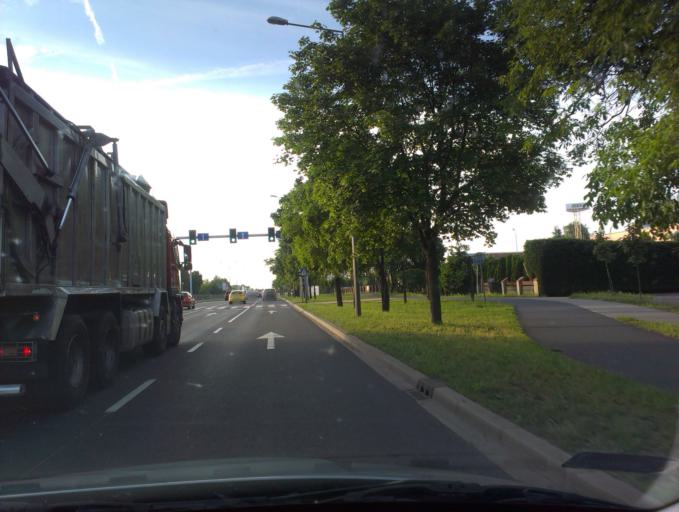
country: PL
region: Greater Poland Voivodeship
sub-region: Leszno
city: Leszno
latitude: 51.8378
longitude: 16.5953
